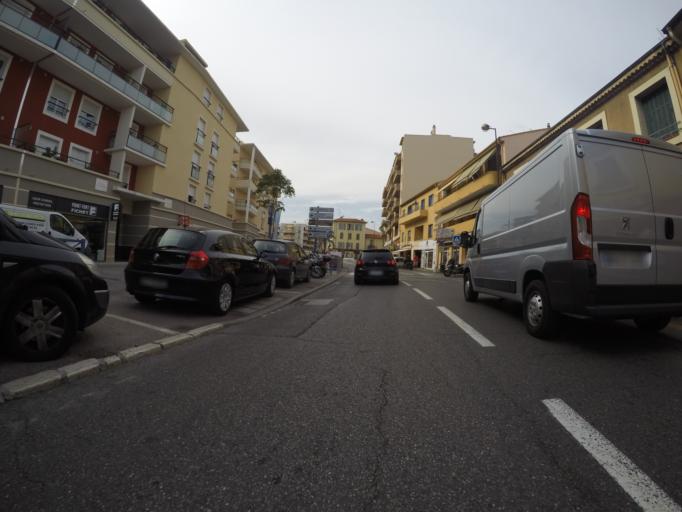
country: FR
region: Provence-Alpes-Cote d'Azur
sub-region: Departement des Alpes-Maritimes
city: Cagnes-sur-Mer
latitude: 43.6644
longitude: 7.1546
